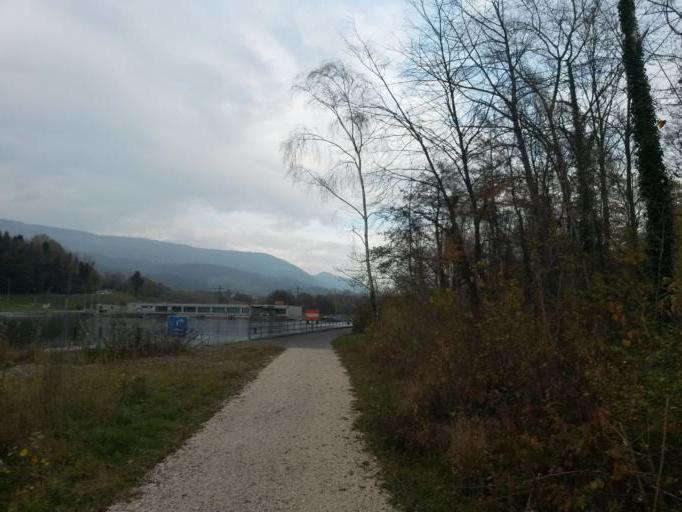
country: CH
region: Solothurn
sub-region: Bezirk Wasseramt
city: Luterbach
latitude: 47.2275
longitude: 7.5883
